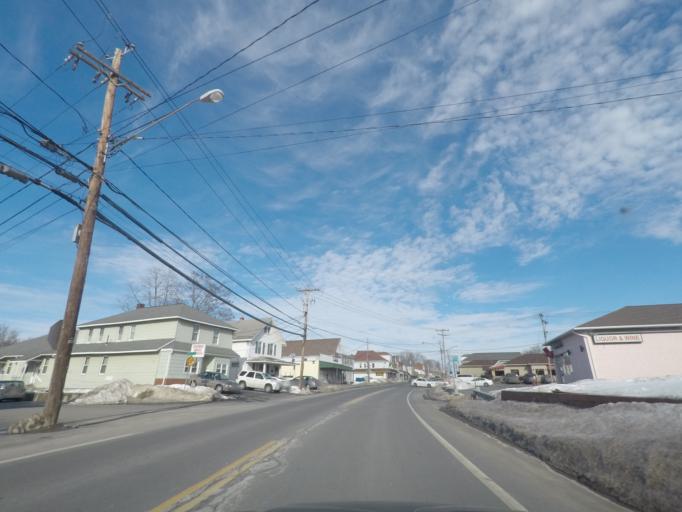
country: US
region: New York
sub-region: Schenectady County
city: Rotterdam
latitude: 42.7937
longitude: -73.9748
